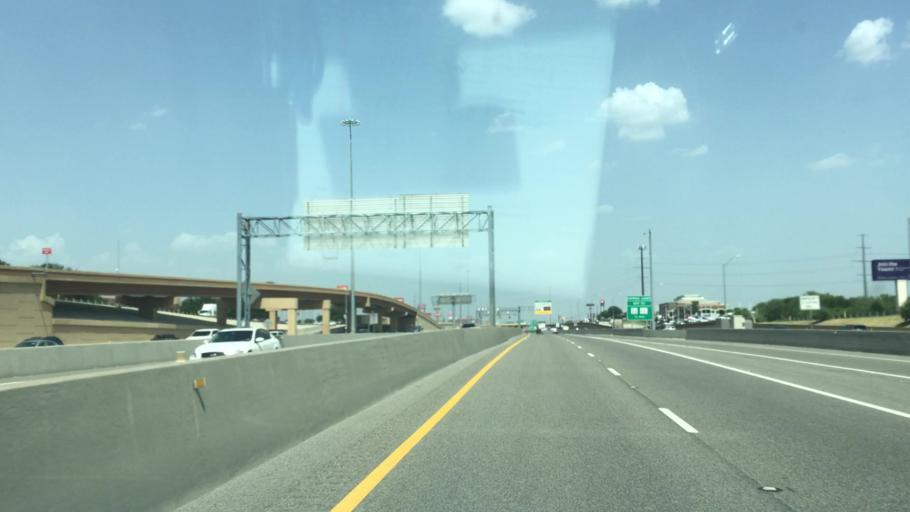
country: US
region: Texas
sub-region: Tarrant County
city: Watauga
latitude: 32.8401
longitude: -97.2475
